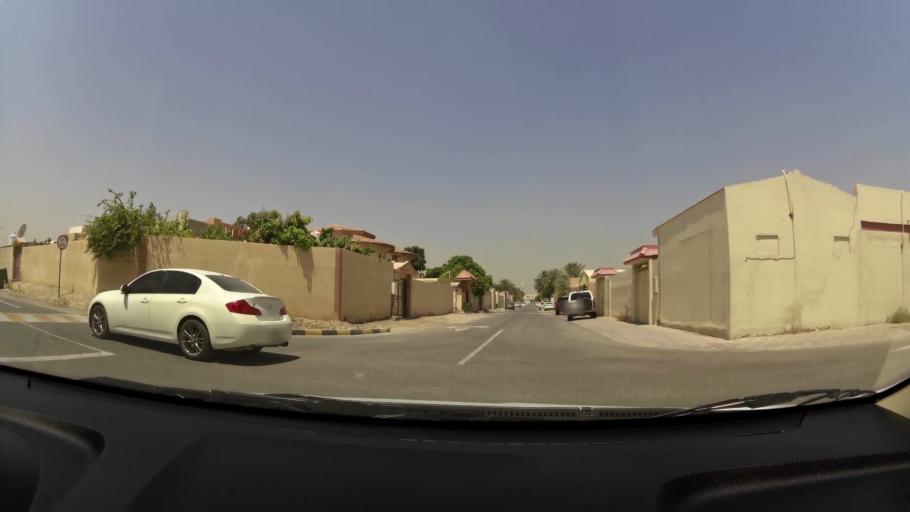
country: AE
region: Ajman
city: Ajman
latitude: 25.4012
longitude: 55.5125
